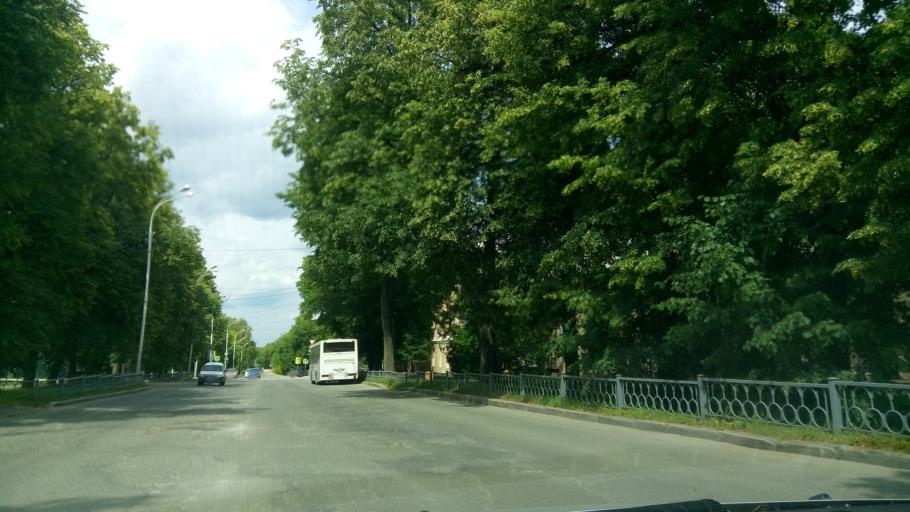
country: RU
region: Sverdlovsk
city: Yekaterinburg
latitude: 56.8862
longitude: 60.6250
